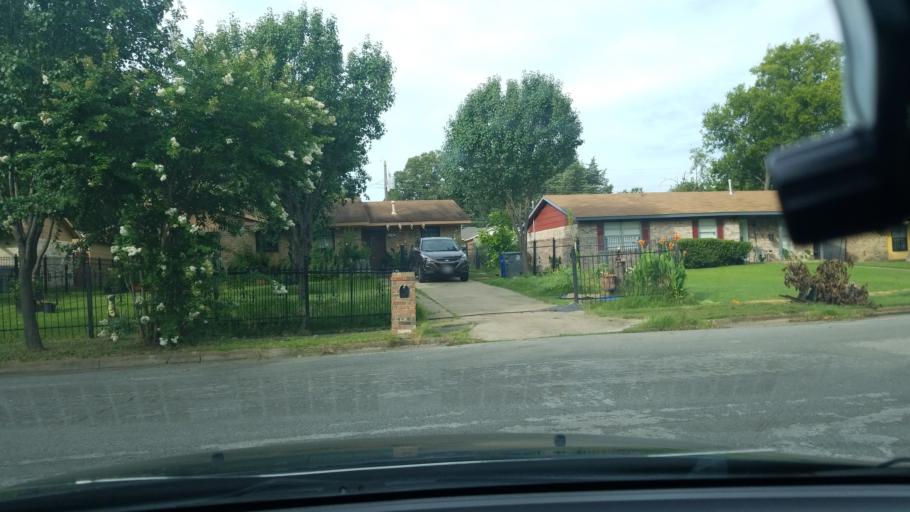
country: US
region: Texas
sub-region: Dallas County
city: Balch Springs
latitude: 32.7533
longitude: -96.6520
